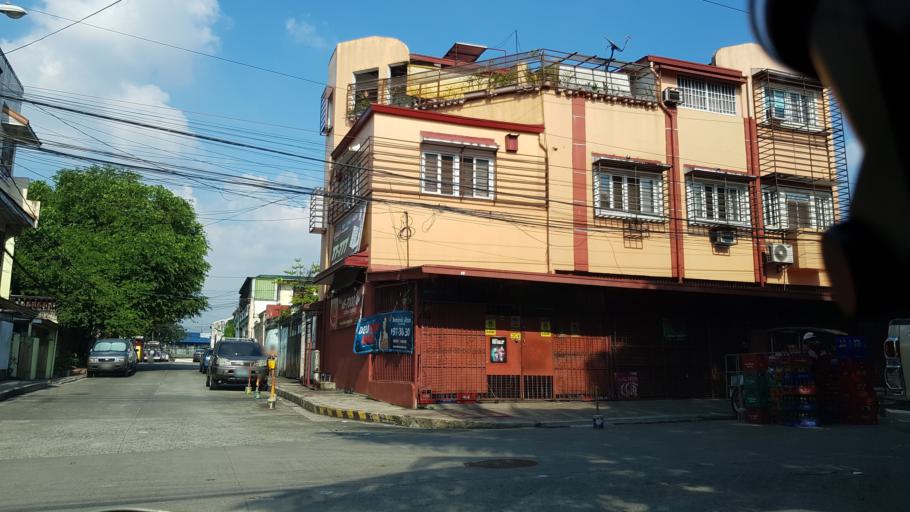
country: PH
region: Metro Manila
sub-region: Quezon City
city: Quezon City
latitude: 14.6292
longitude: 121.0437
